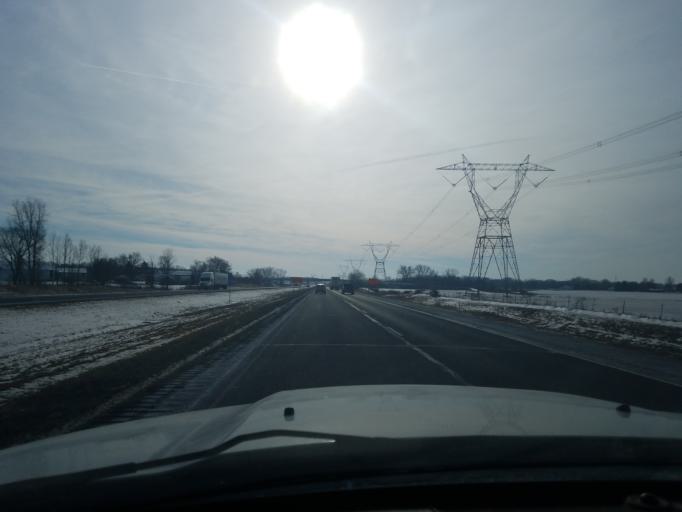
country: US
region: Indiana
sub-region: Huntington County
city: Roanoke
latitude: 40.9349
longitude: -85.3114
